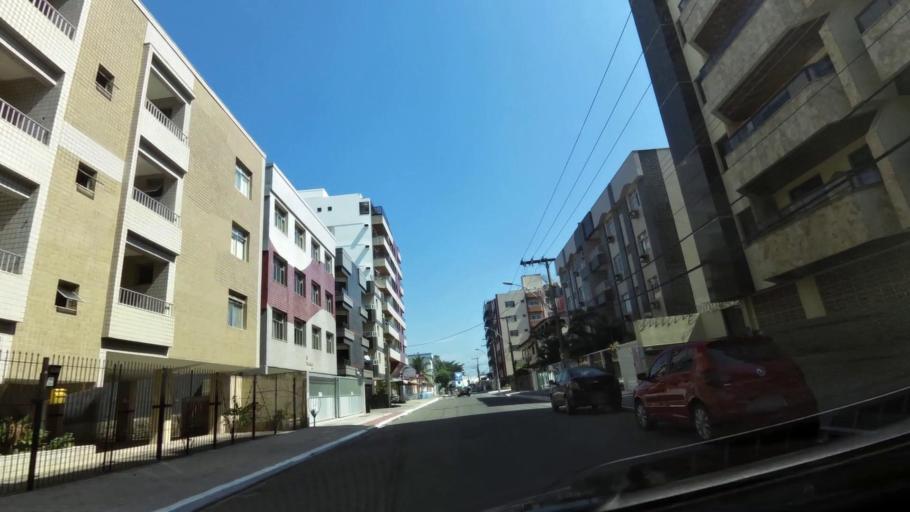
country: BR
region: Espirito Santo
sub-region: Guarapari
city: Guarapari
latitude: -20.6573
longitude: -40.4945
